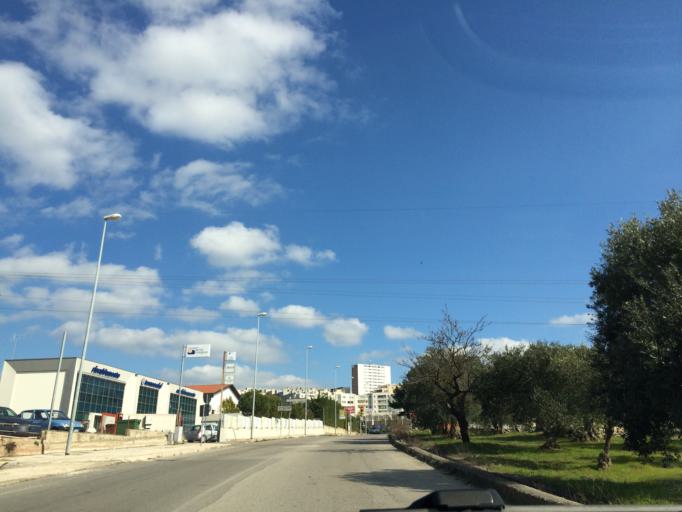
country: IT
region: Basilicate
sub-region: Provincia di Matera
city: Matera
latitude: 40.6693
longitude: 16.5754
